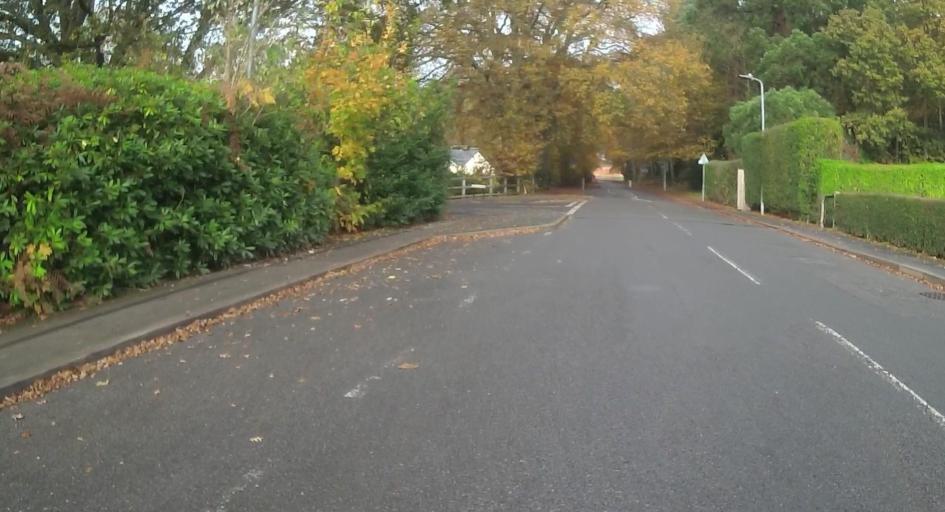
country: GB
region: England
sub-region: Bracknell Forest
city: Crowthorne
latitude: 51.3658
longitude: -0.7831
